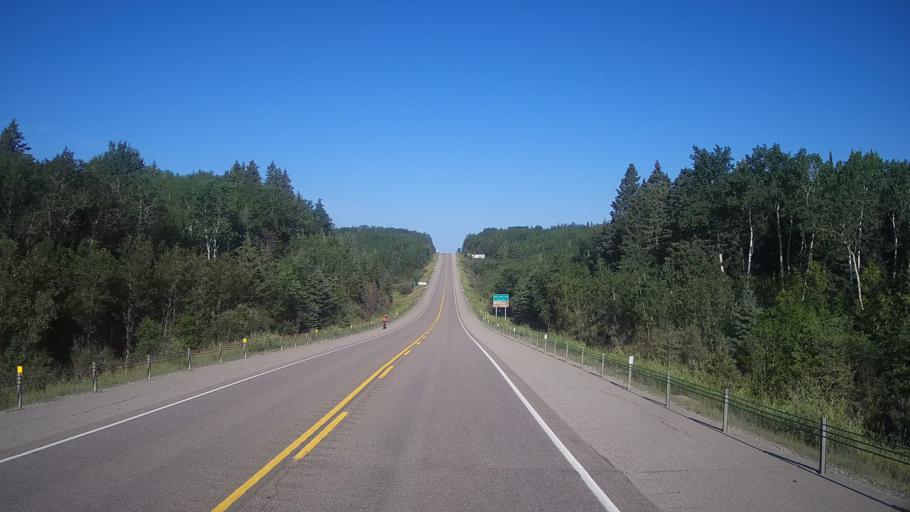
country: US
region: Minnesota
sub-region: Roseau County
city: Warroad
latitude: 49.7373
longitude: -95.1930
